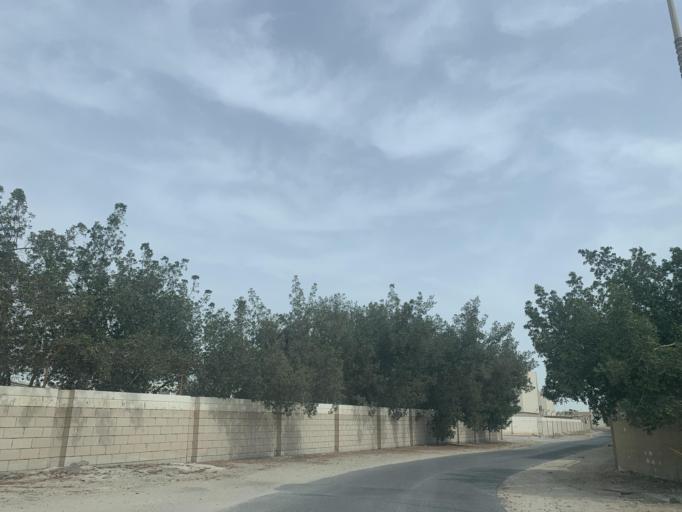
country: BH
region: Northern
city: Madinat `Isa
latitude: 26.1579
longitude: 50.5445
